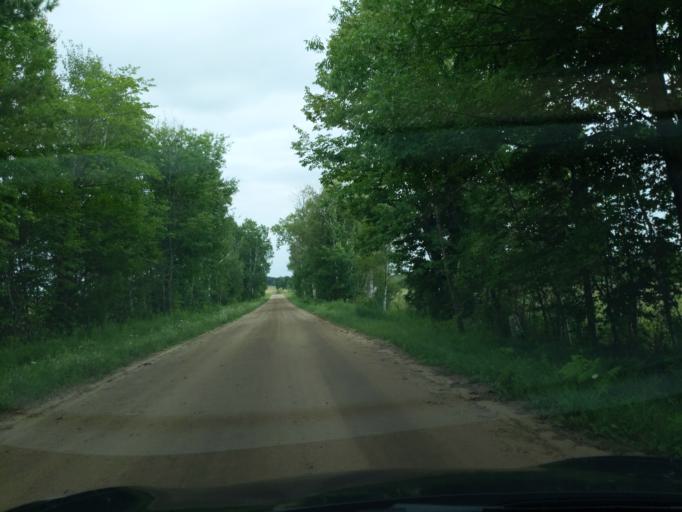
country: US
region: Michigan
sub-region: Clare County
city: Harrison
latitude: 43.9878
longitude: -85.0017
